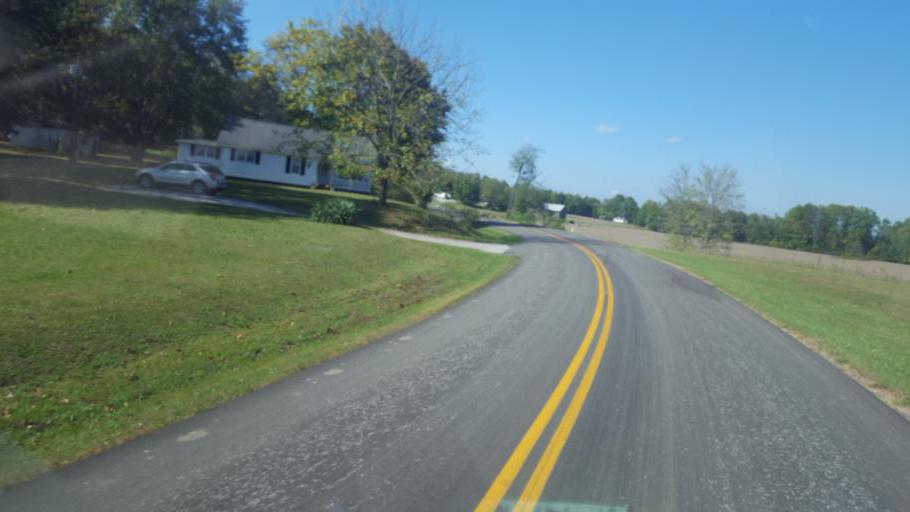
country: US
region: Kentucky
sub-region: Fleming County
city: Flemingsburg
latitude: 38.4622
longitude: -83.5843
